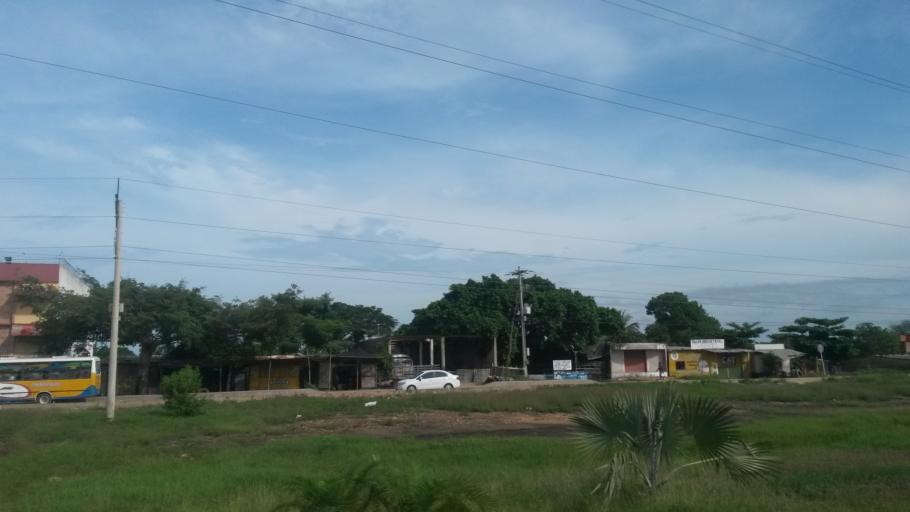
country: CO
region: Bolivar
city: Cartagena
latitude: 10.4063
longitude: -75.4516
